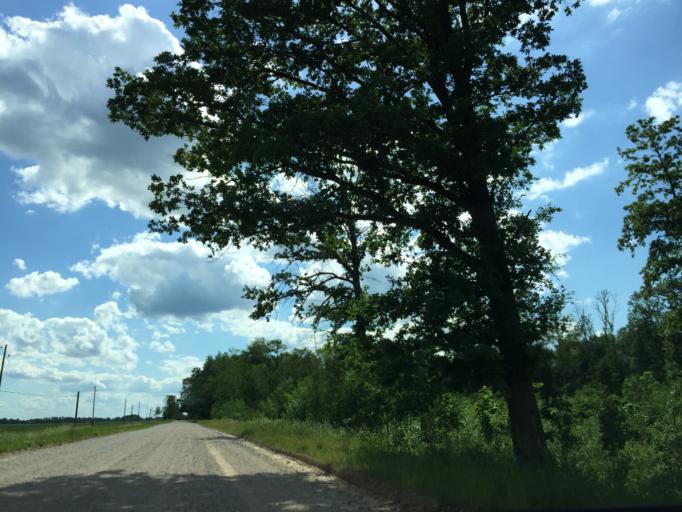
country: LV
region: Engure
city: Smarde
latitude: 56.8639
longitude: 23.3221
